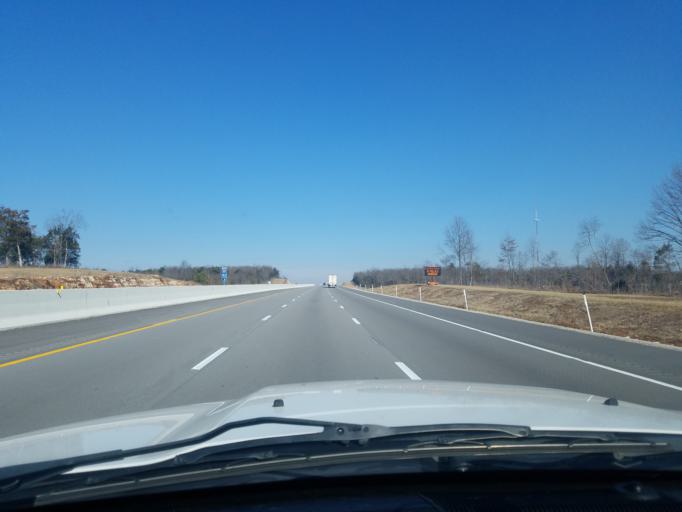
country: US
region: Kentucky
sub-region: Hart County
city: Munfordville
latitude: 37.4418
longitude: -85.8838
